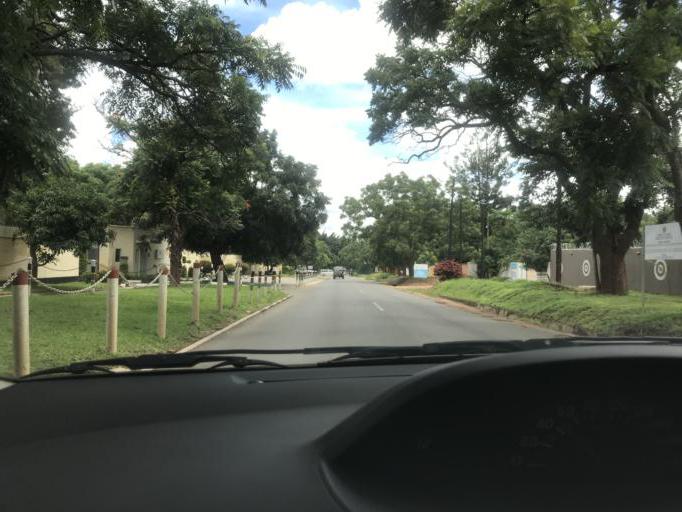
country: ZM
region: Lusaka
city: Lusaka
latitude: -15.4222
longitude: 28.3122
